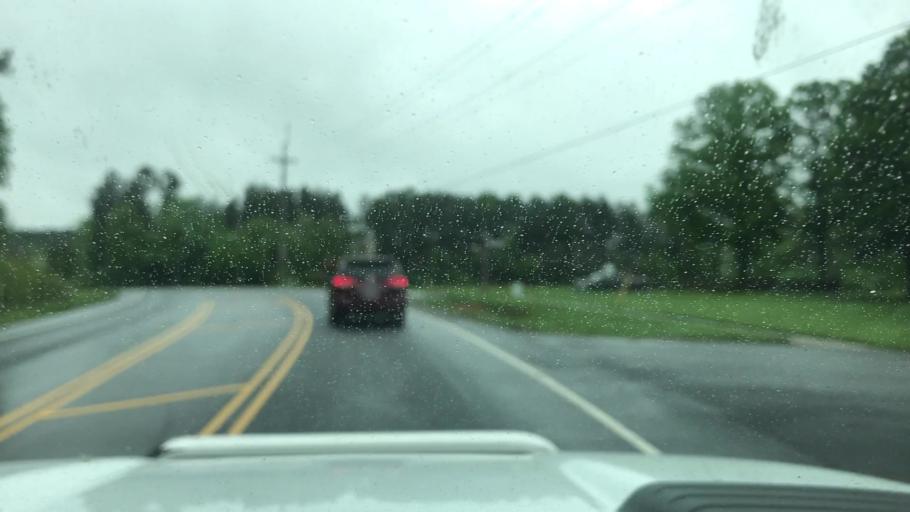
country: US
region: North Carolina
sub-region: Mecklenburg County
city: Huntersville
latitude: 35.3992
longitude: -80.8699
